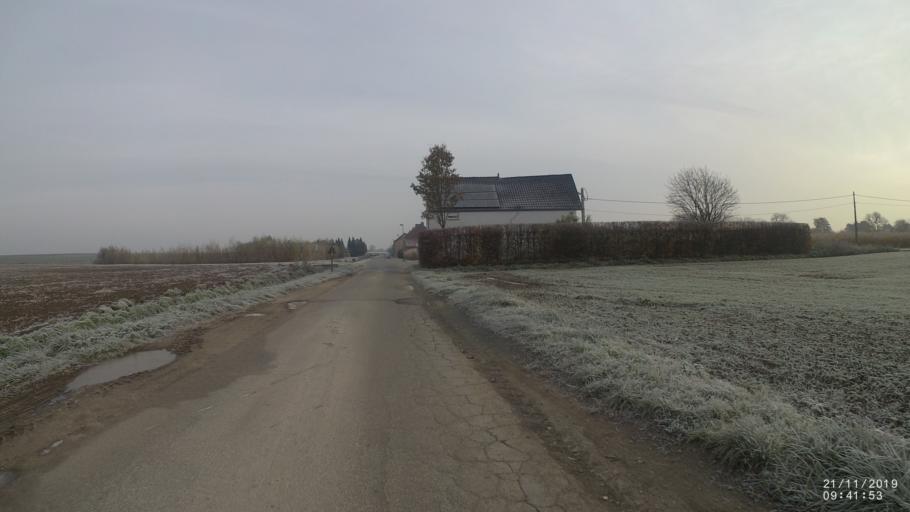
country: BE
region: Flanders
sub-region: Provincie Vlaams-Brabant
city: Tienen
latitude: 50.7797
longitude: 4.9967
